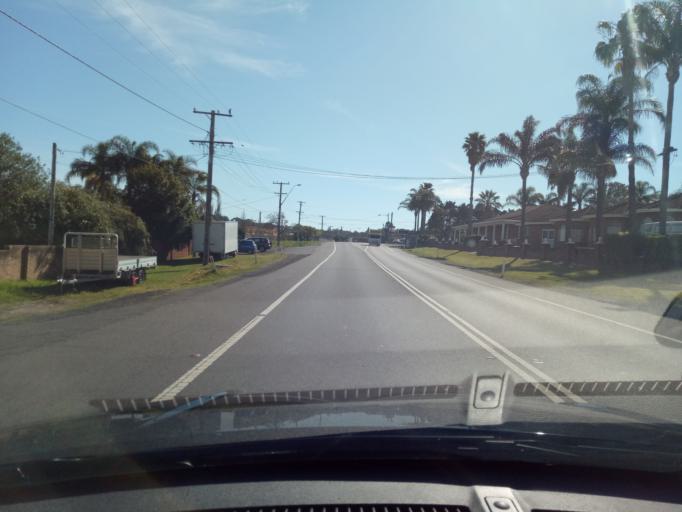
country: AU
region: New South Wales
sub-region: Gosford Shire
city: Forresters Beach
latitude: -33.4068
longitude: 151.4641
